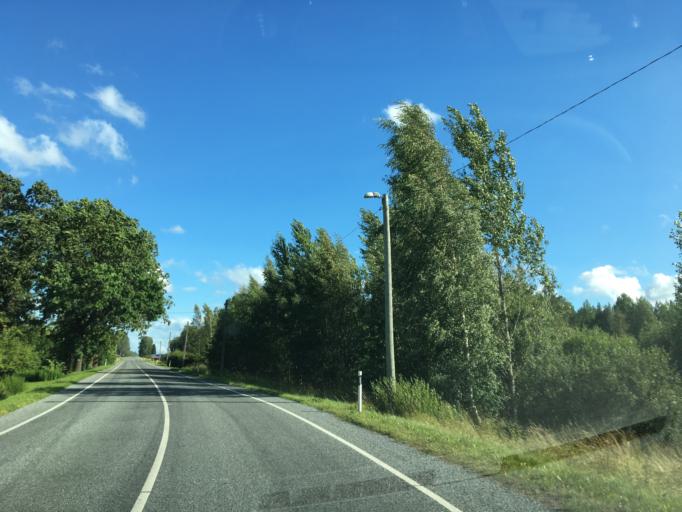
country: EE
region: Paernumaa
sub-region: Vaendra vald (alev)
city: Vandra
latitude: 58.6153
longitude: 25.1034
